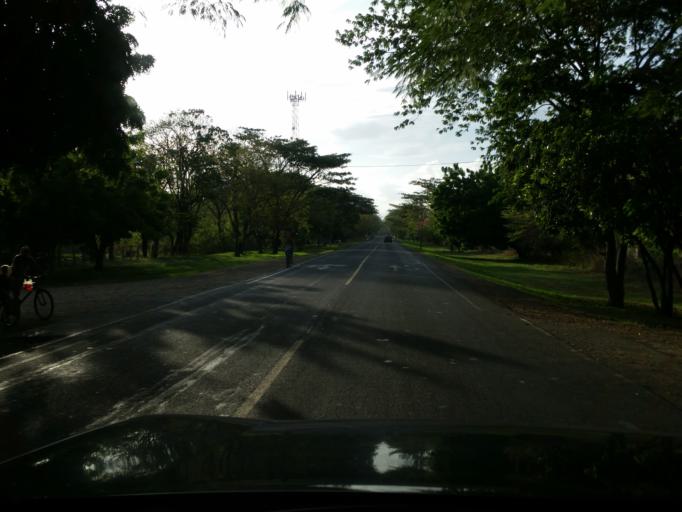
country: NI
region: Rivas
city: Belen
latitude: 11.6162
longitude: -85.9462
